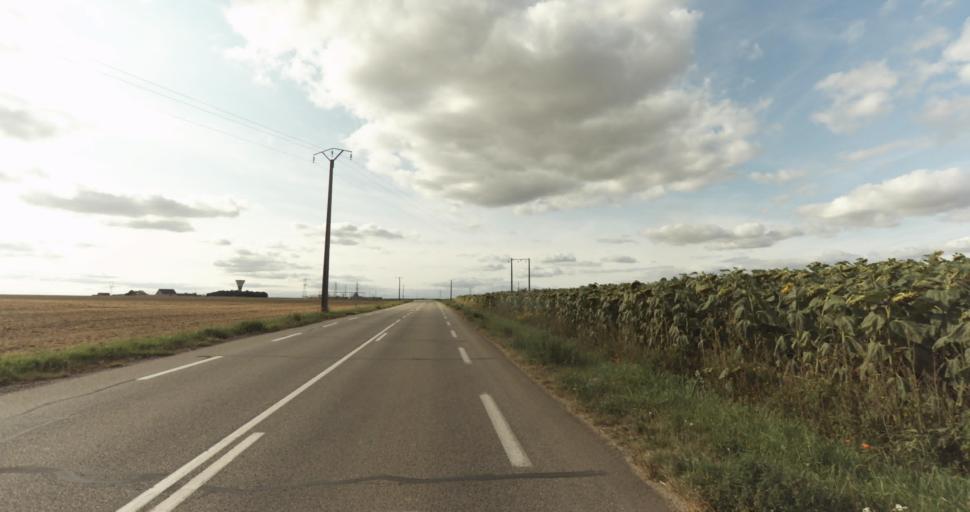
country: FR
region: Haute-Normandie
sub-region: Departement de l'Eure
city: Ivry-la-Bataille
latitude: 48.8878
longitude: 1.4442
